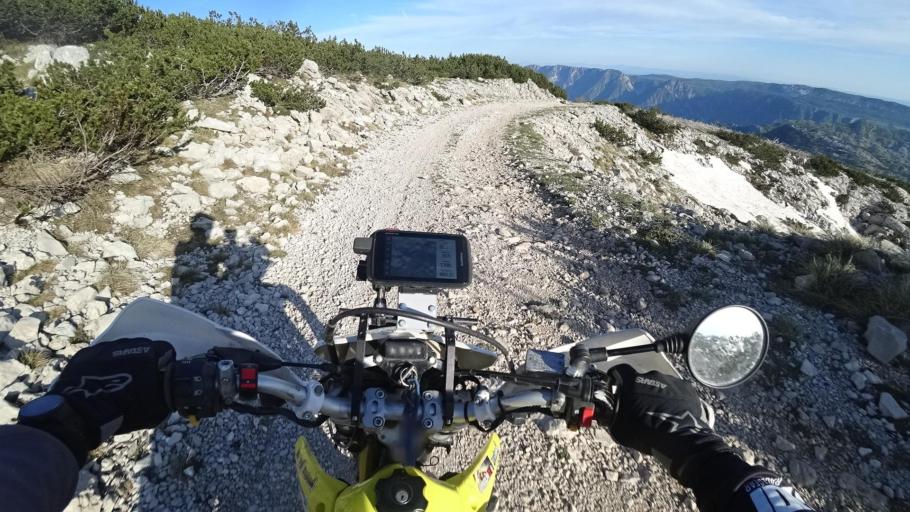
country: BA
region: Federation of Bosnia and Herzegovina
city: Kocerin
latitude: 43.5930
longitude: 17.5393
